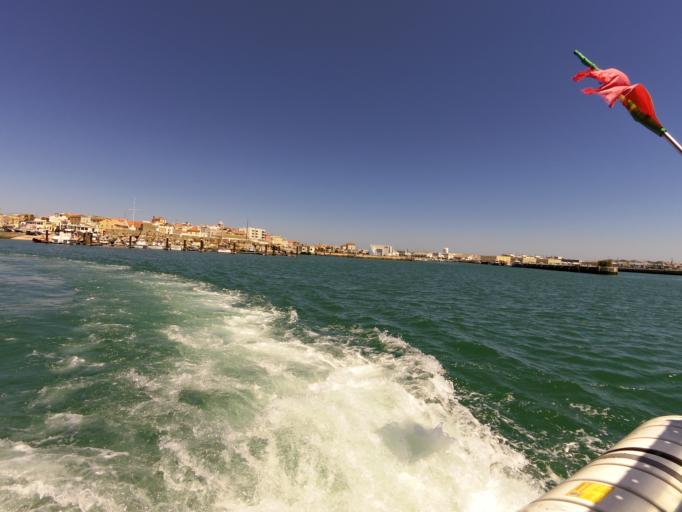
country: PT
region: Leiria
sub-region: Peniche
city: Peniche
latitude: 39.3525
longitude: -9.3769
